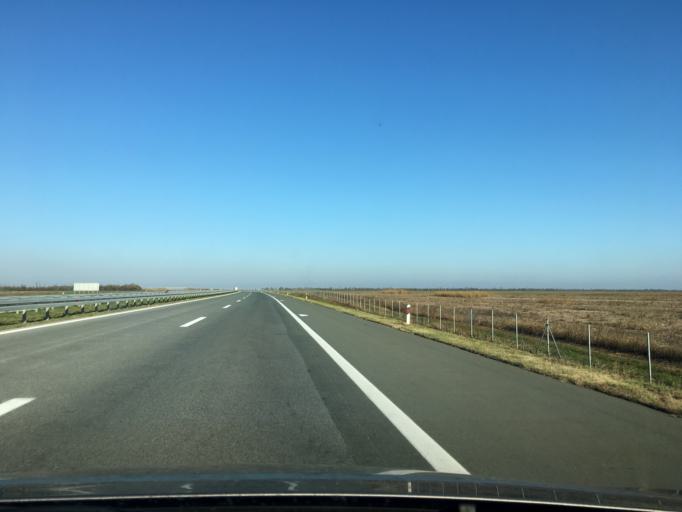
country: RS
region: Autonomna Pokrajina Vojvodina
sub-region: Severnobacki Okrug
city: Mali Igos
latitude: 45.6815
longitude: 19.7283
